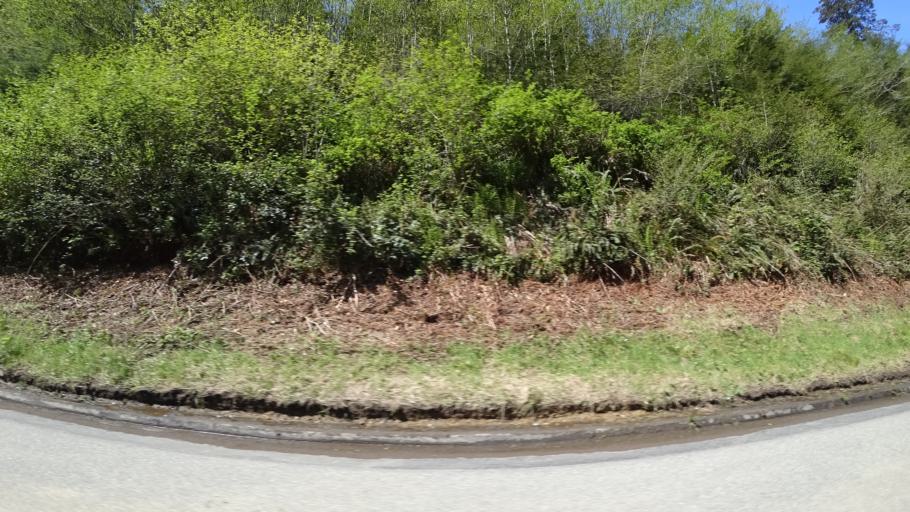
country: US
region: California
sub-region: Del Norte County
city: Bertsch-Oceanview
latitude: 41.4345
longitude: -124.0225
